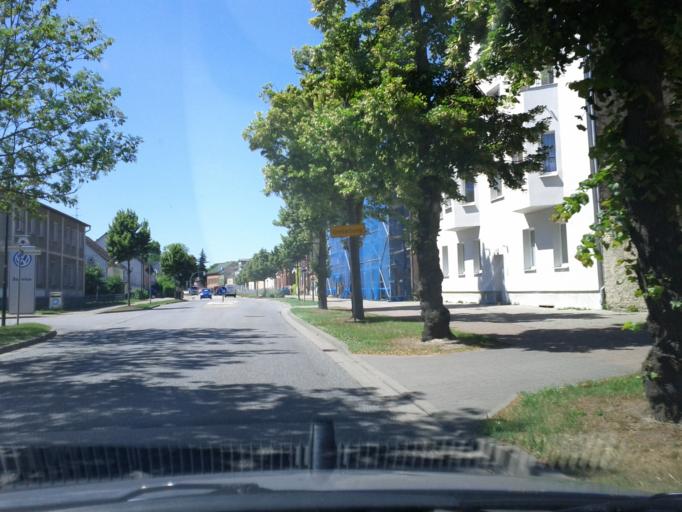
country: DE
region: Brandenburg
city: Rehfelde
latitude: 52.4817
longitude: 13.8533
